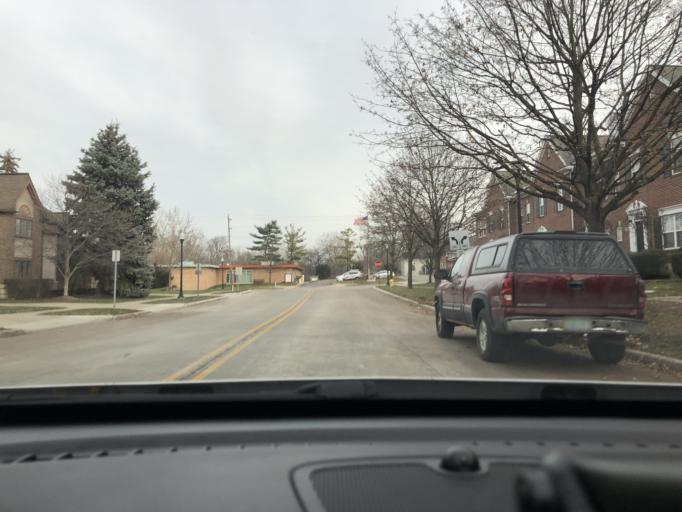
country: US
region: Michigan
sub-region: Wayne County
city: Dearborn Heights
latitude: 42.3080
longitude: -83.2413
